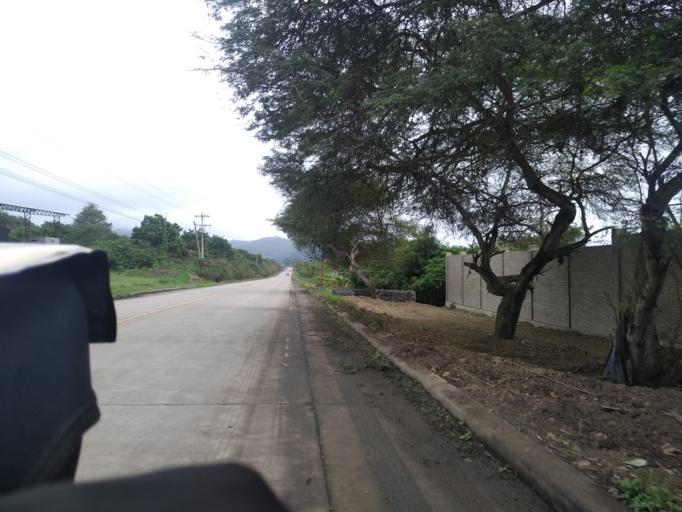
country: EC
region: Manabi
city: Jipijapa
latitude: -1.6565
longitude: -80.8196
